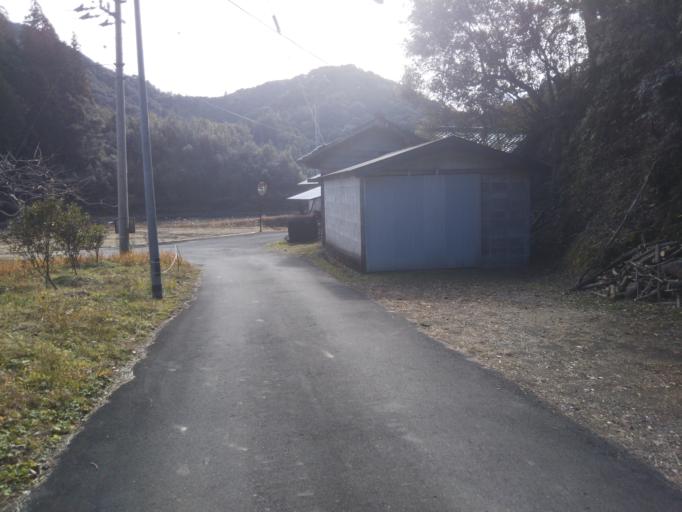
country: JP
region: Kochi
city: Nakamura
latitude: 33.0462
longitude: 132.9877
